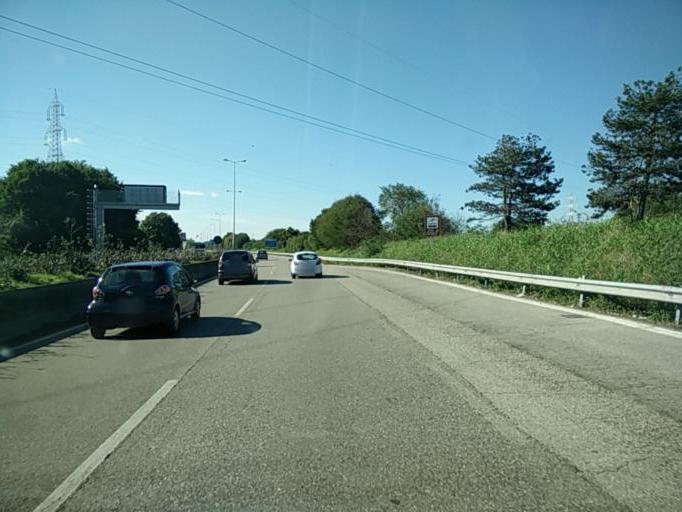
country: IT
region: Veneto
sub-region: Provincia di Verona
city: Caselle
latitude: 45.4318
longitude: 10.9220
